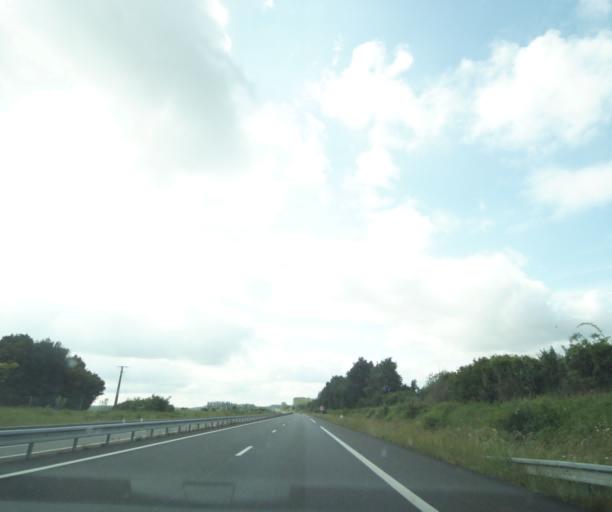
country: FR
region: Pays de la Loire
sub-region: Departement de Maine-et-Loire
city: Vivy
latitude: 47.3571
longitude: -0.0799
